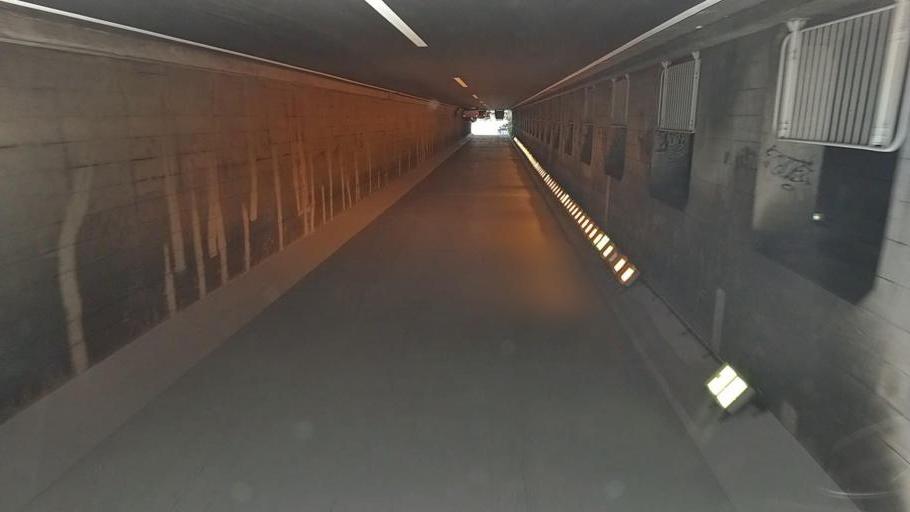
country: JP
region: Kanagawa
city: Minami-rinkan
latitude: 35.4761
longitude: 139.5030
